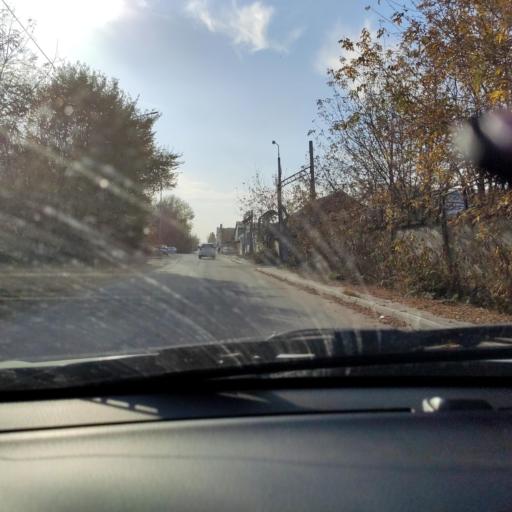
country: RU
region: Tatarstan
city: Verkhniy Uslon
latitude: 55.8030
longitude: 49.0473
